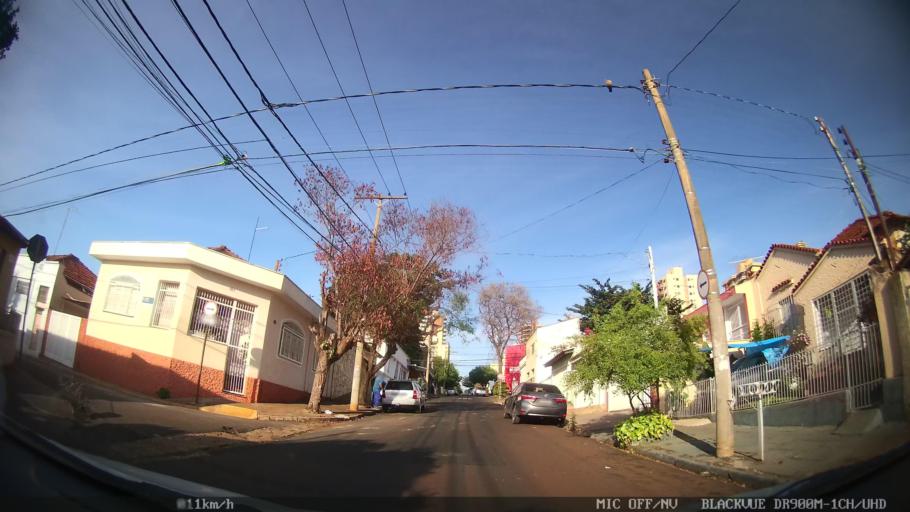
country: BR
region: Sao Paulo
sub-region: Ribeirao Preto
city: Ribeirao Preto
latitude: -21.1859
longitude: -47.8004
